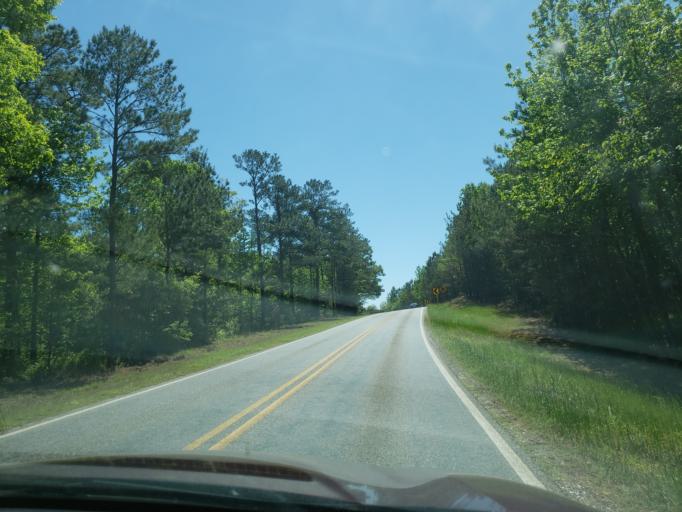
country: US
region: Alabama
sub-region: Tallapoosa County
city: Dadeville
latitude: 32.7061
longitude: -85.8191
